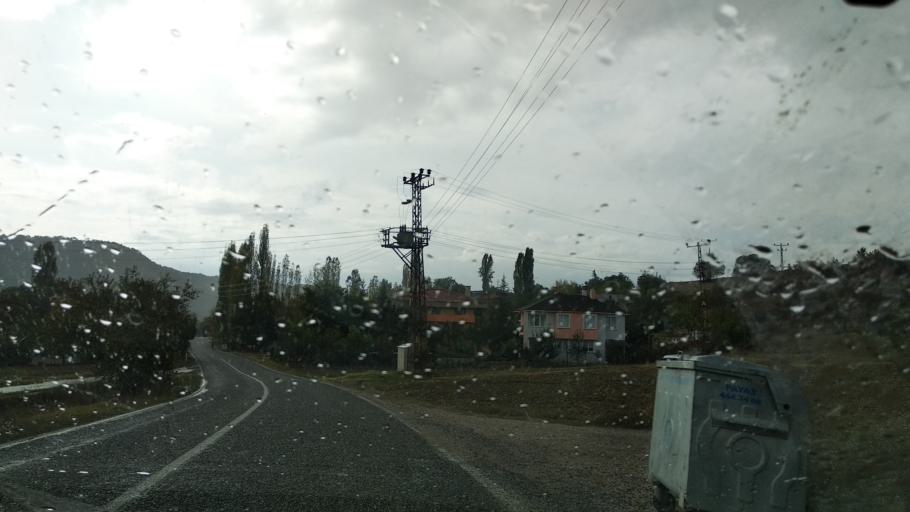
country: TR
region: Ankara
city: Nallihan
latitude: 40.3326
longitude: 31.4129
